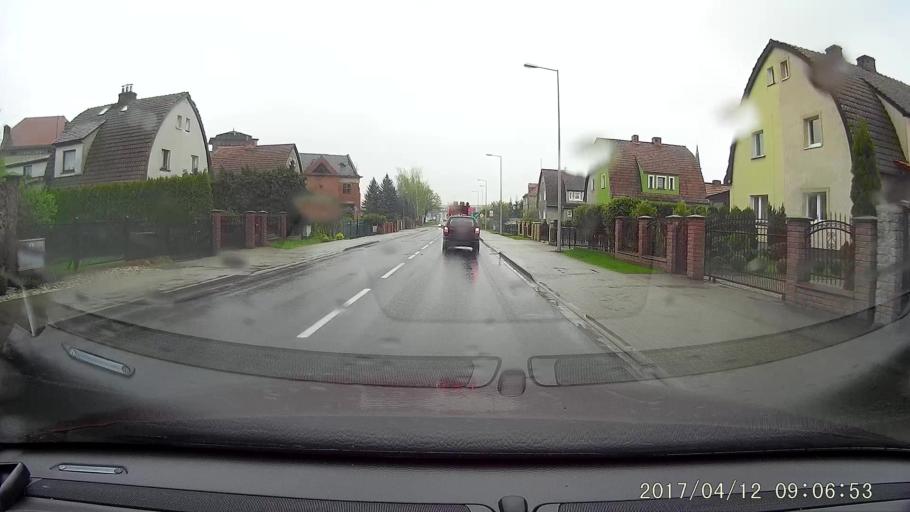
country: PL
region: Lower Silesian Voivodeship
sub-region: Powiat zgorzelecki
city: Zgorzelec
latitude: 51.1547
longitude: 15.0231
